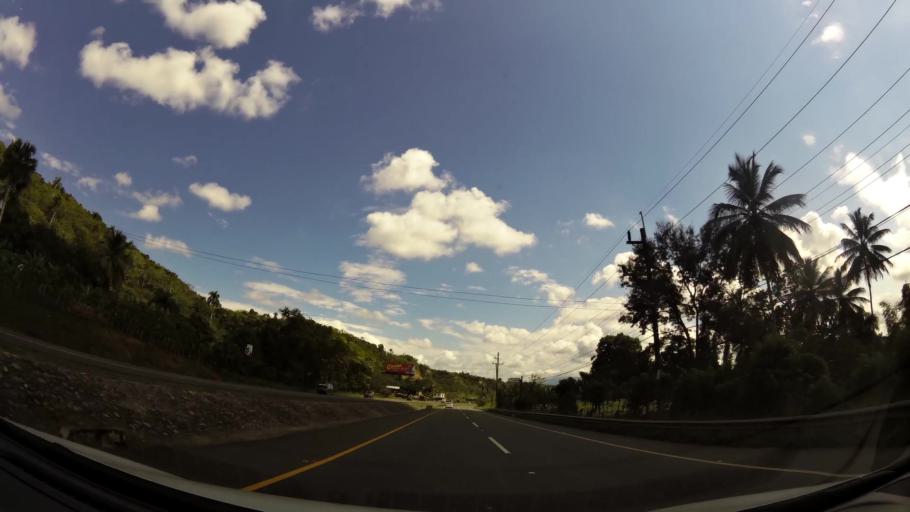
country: DO
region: La Vega
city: Rio Verde Arriba
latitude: 19.2810
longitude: -70.5713
